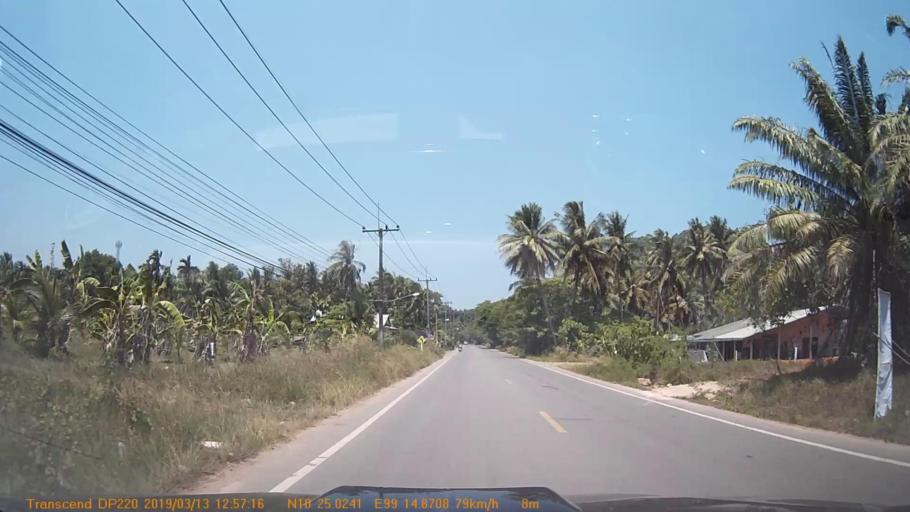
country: TH
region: Chumphon
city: Chumphon
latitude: 10.4176
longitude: 99.2479
